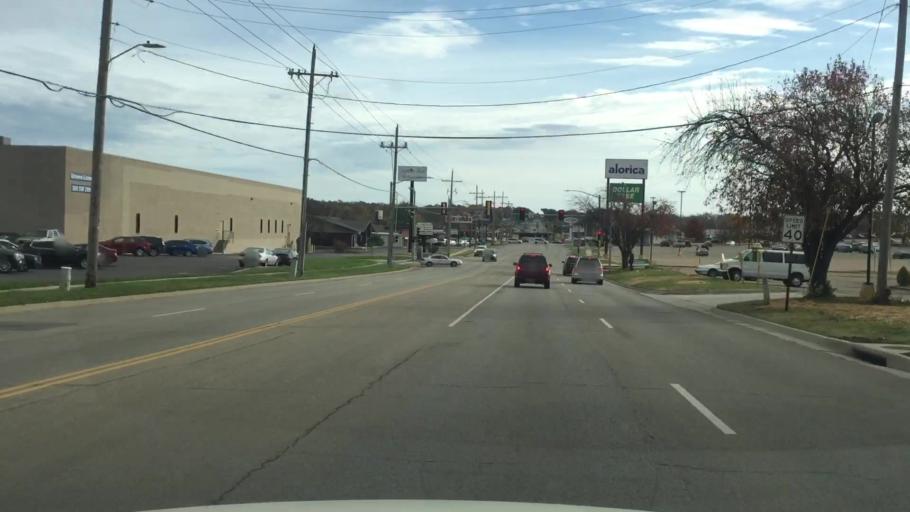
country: US
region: Kansas
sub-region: Shawnee County
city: Topeka
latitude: 39.0151
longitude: -95.6854
